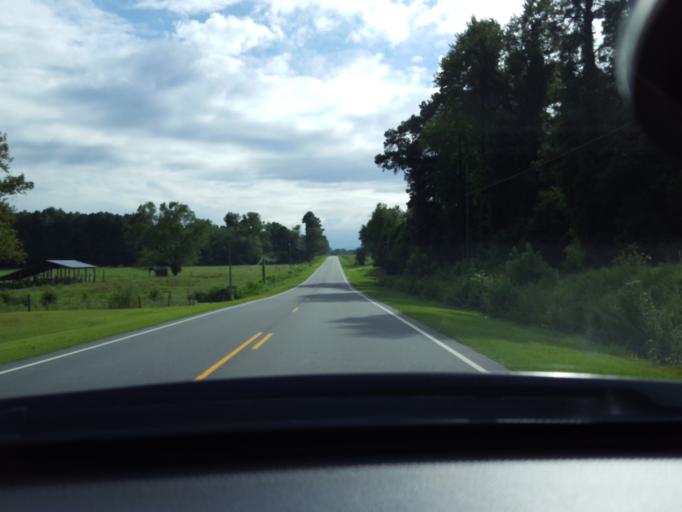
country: US
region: North Carolina
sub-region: Duplin County
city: Kenansville
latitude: 35.0013
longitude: -77.9158
